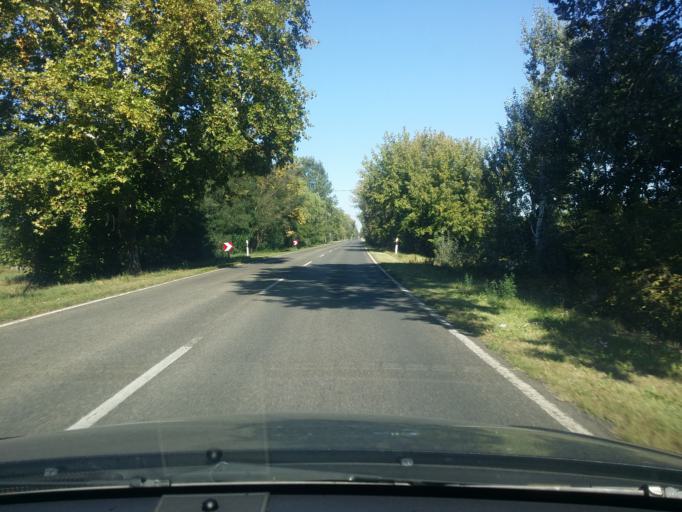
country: HU
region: Csongrad
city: Kistelek
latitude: 46.4913
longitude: 19.9626
